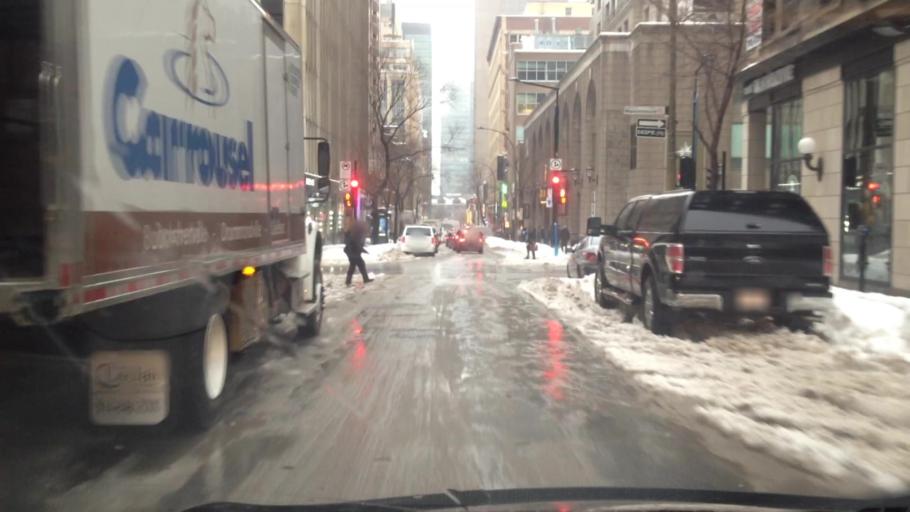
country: CA
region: Quebec
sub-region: Montreal
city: Montreal
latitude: 45.5005
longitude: -73.5759
